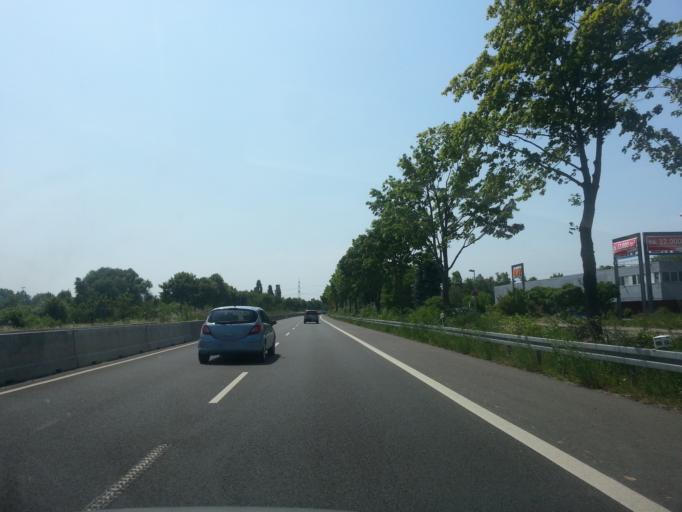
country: DE
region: Hesse
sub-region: Regierungsbezirk Darmstadt
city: Bensheim
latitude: 49.6710
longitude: 8.5952
